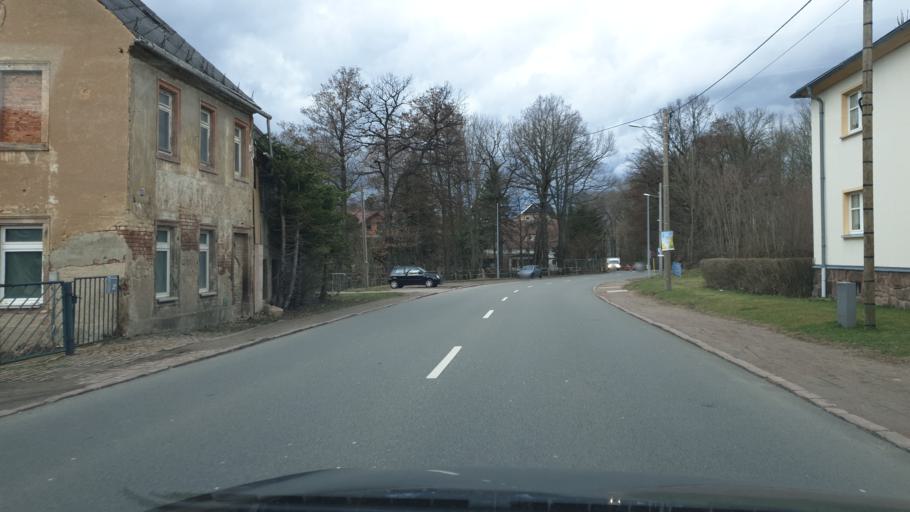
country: DE
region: Saxony
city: Mittweida
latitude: 50.9750
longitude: 12.9727
